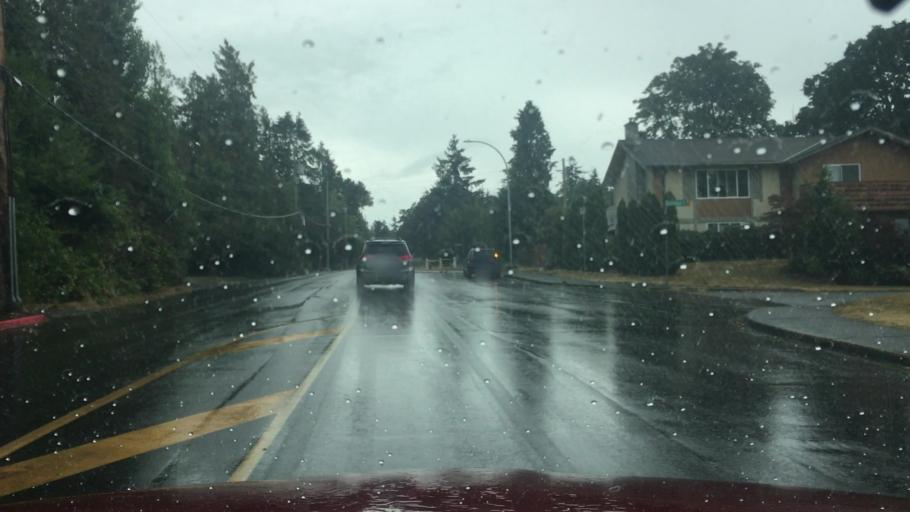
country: CA
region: British Columbia
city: Victoria
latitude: 48.4713
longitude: -123.3510
